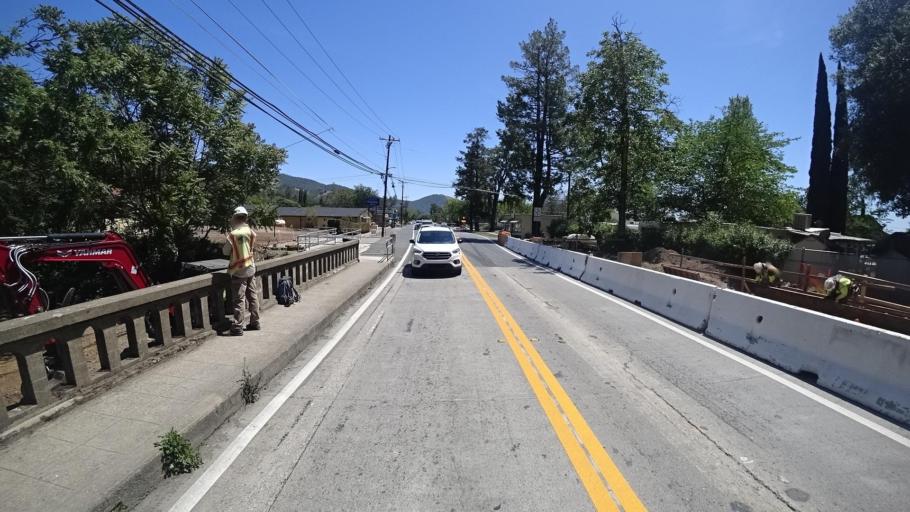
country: US
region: California
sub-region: Lake County
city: Lucerne
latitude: 39.0959
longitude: -122.8014
